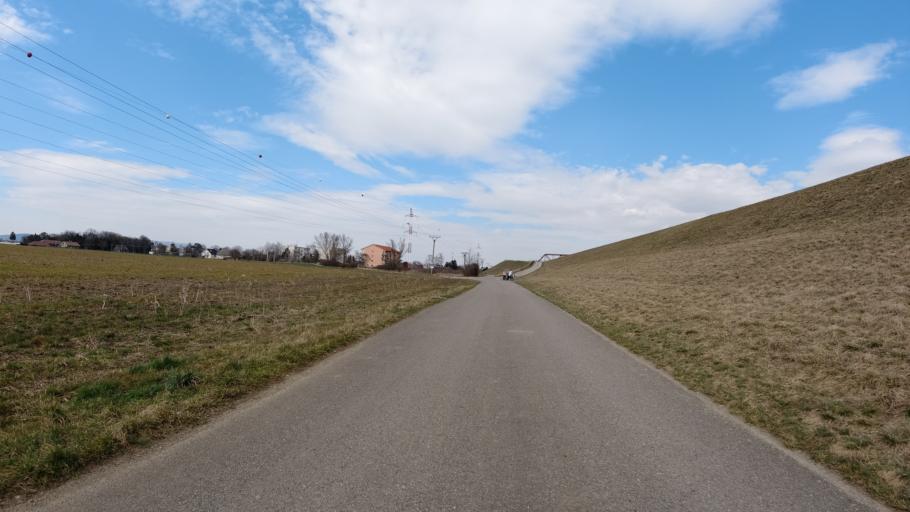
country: SK
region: Trnavsky
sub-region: Okres Trnava
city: Piestany
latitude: 48.6679
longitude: 17.8577
